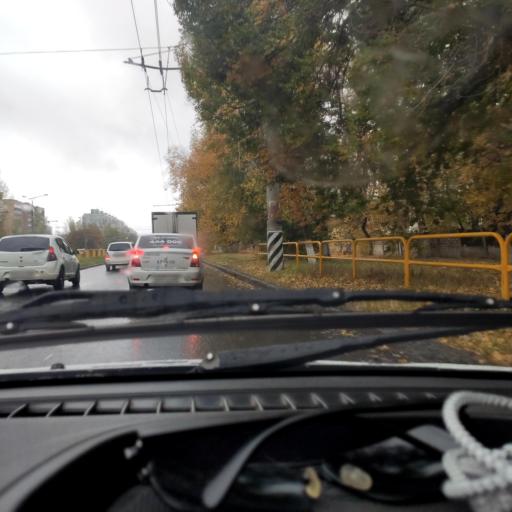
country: RU
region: Samara
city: Zhigulevsk
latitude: 53.4838
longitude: 49.4739
